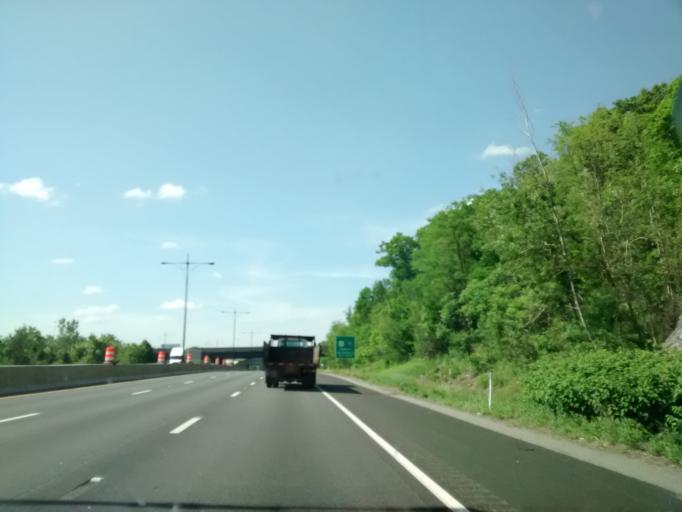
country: US
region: Massachusetts
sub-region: Worcester County
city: Millbury
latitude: 42.2082
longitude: -71.7803
